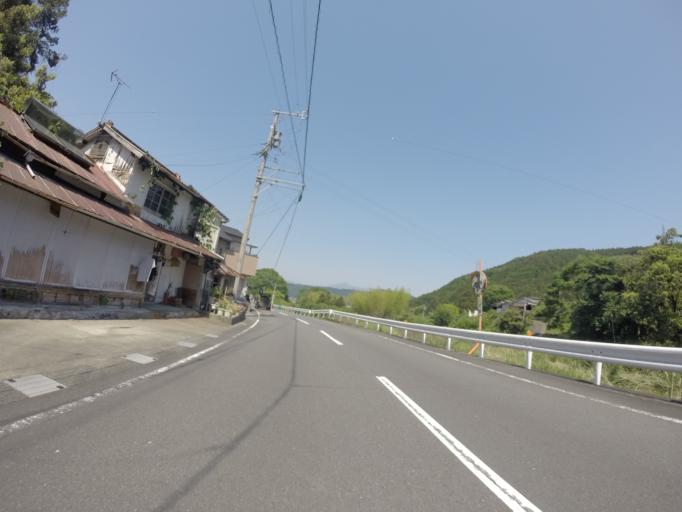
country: JP
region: Shizuoka
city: Fujinomiya
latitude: 35.1843
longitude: 138.5863
